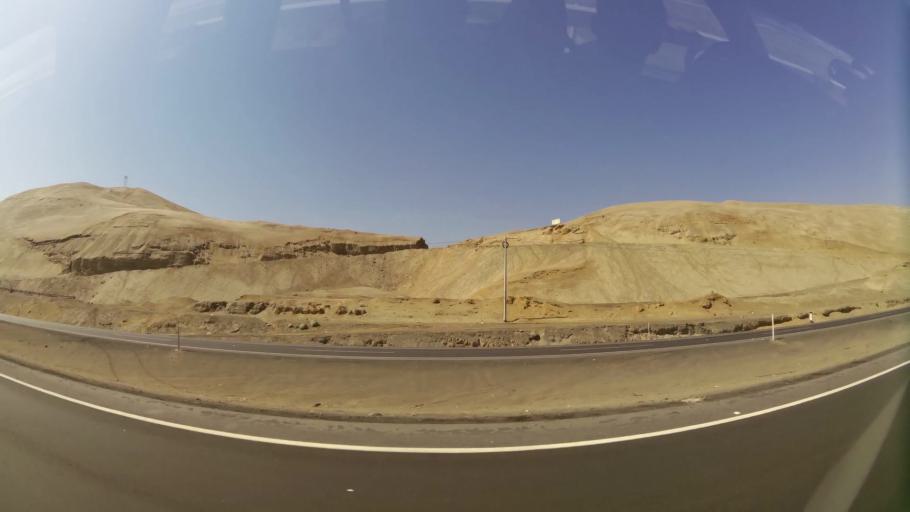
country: PE
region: Ica
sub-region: Provincia de Chincha
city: San Pedro
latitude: -13.3181
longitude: -76.2461
